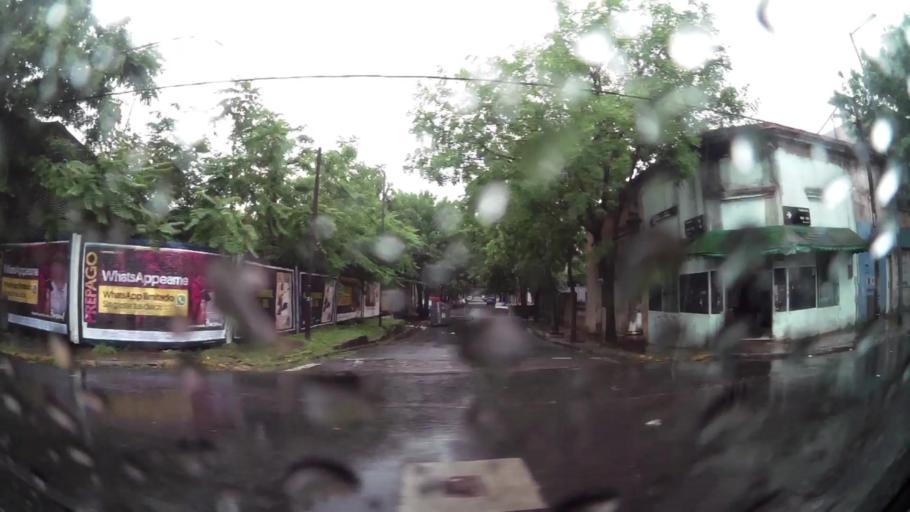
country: AR
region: Buenos Aires
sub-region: Partido de Avellaneda
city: Avellaneda
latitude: -34.6440
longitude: -58.3610
